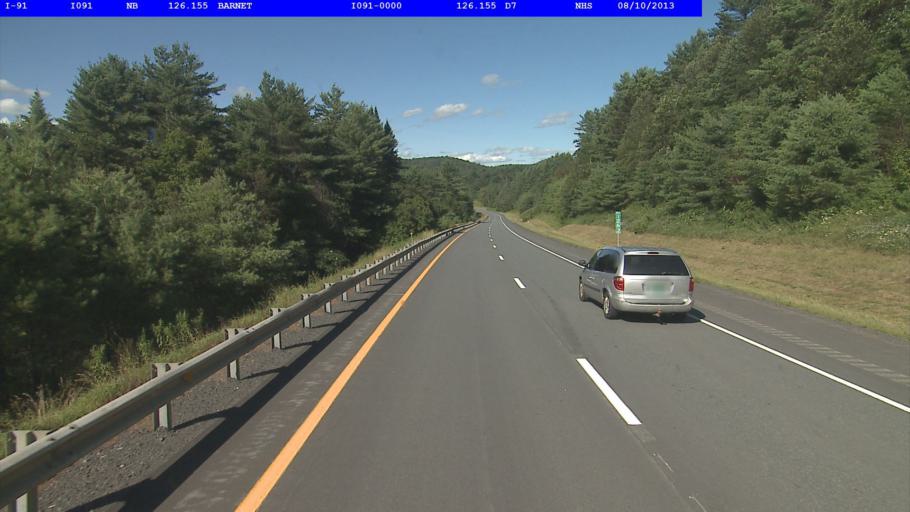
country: US
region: Vermont
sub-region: Caledonia County
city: Saint Johnsbury
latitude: 44.3680
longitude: -72.0274
